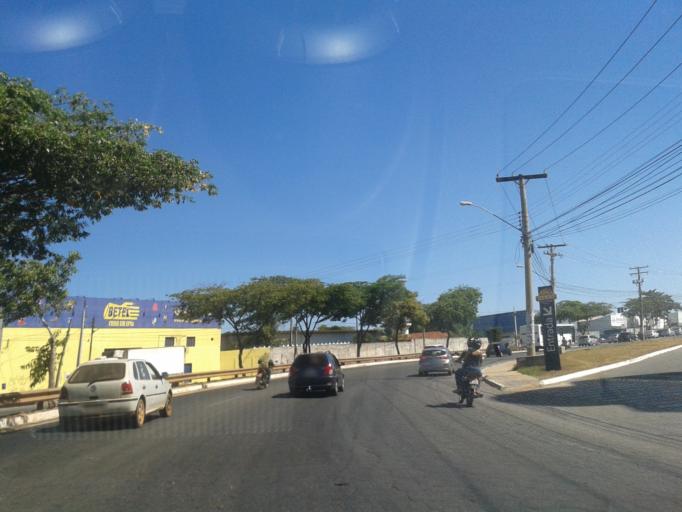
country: BR
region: Goias
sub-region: Goiania
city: Goiania
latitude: -16.6516
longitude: -49.3171
